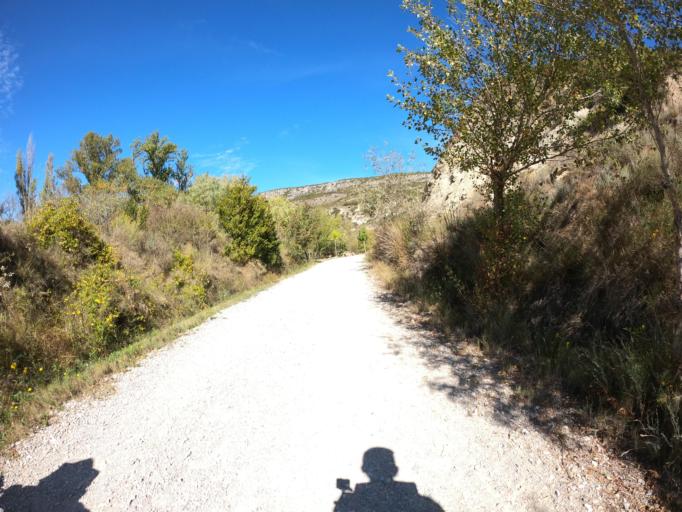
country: ES
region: Navarre
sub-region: Provincia de Navarra
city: Liedena
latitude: 42.6206
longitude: -1.2889
